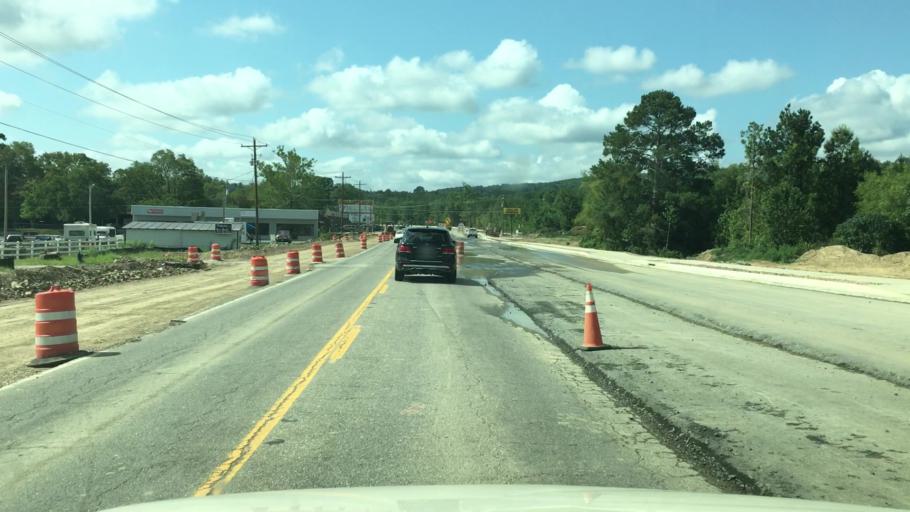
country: US
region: Arkansas
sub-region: Garland County
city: Lake Hamilton
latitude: 34.4224
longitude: -93.0977
